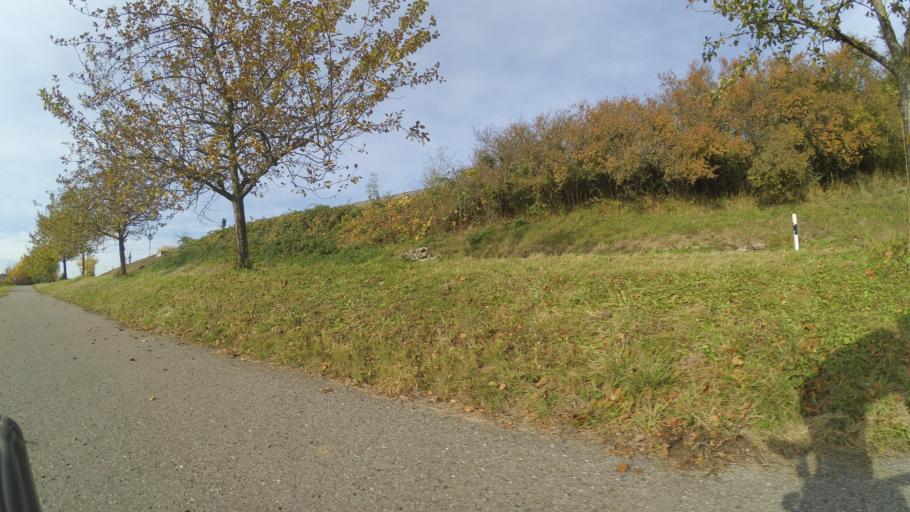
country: DE
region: Baden-Wuerttemberg
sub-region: Regierungsbezirk Stuttgart
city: Ohringen
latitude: 49.2036
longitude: 9.5339
